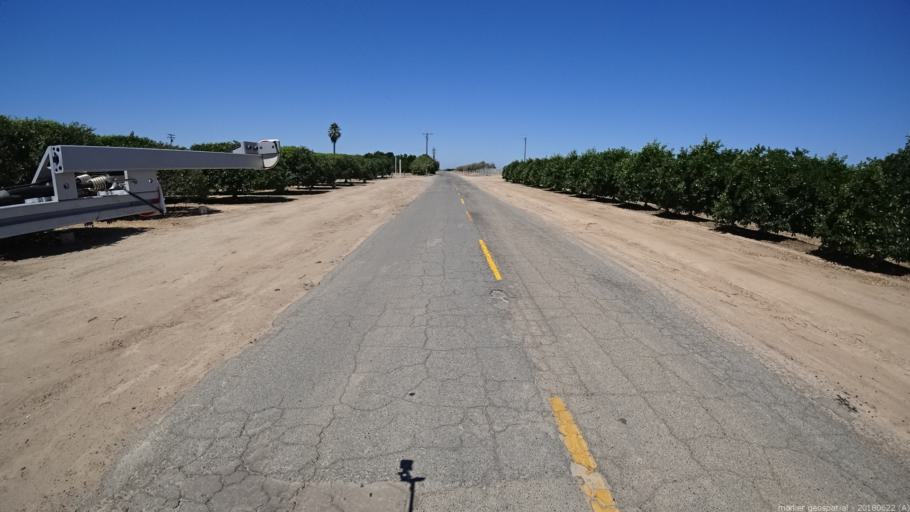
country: US
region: California
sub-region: Madera County
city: Bonadelle Ranchos-Madera Ranchos
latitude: 36.8949
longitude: -119.8386
